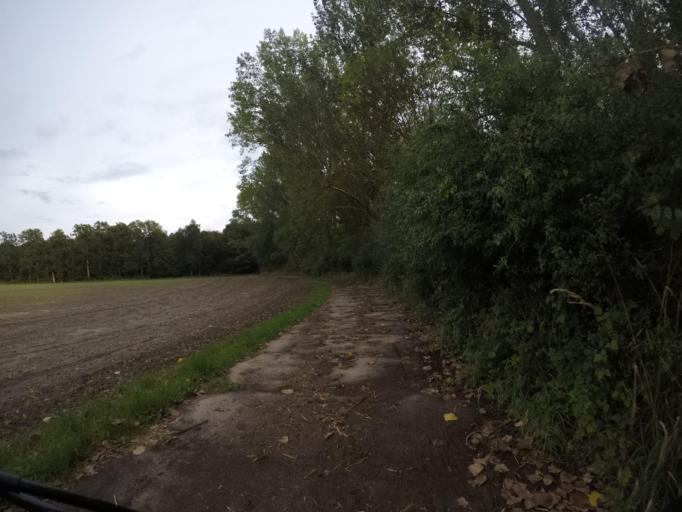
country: DE
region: Lower Saxony
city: Neu Darchau
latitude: 53.2798
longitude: 10.8844
